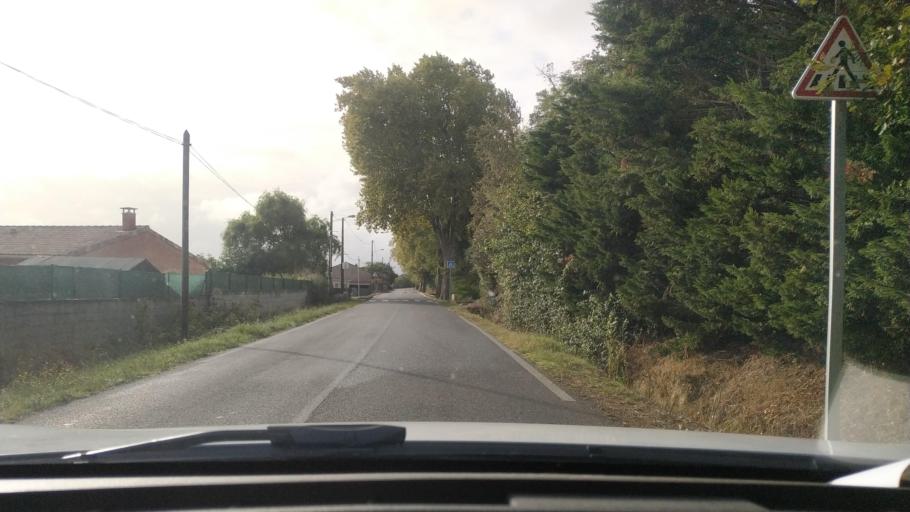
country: FR
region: Midi-Pyrenees
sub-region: Departement de la Haute-Garonne
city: Gaillac-Toulza
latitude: 43.3023
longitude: 1.4682
